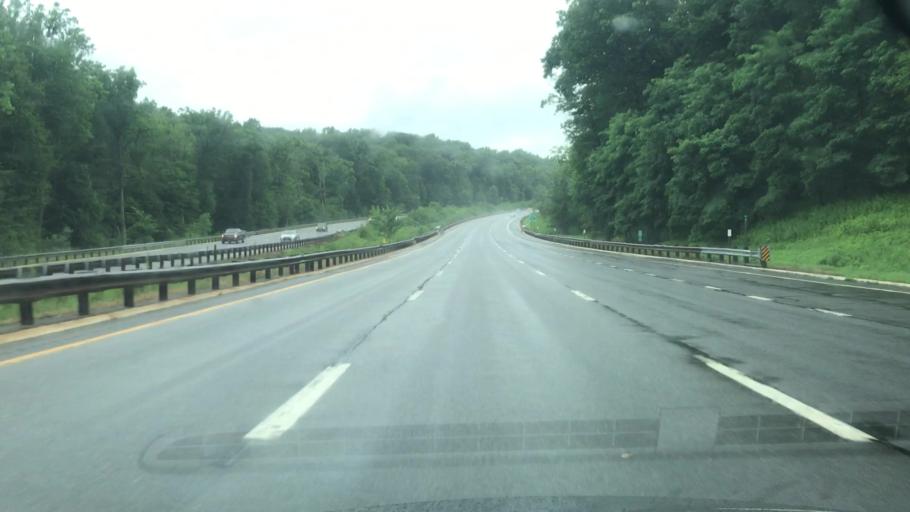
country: US
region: New York
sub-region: Westchester County
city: Shrub Oak
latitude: 41.3020
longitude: -73.8235
